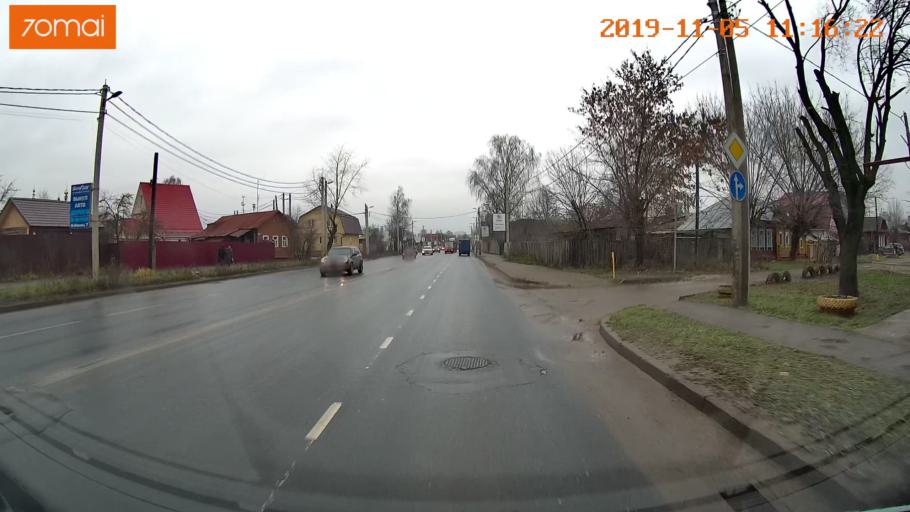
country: RU
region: Ivanovo
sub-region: Gorod Ivanovo
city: Ivanovo
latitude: 56.9843
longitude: 40.9534
